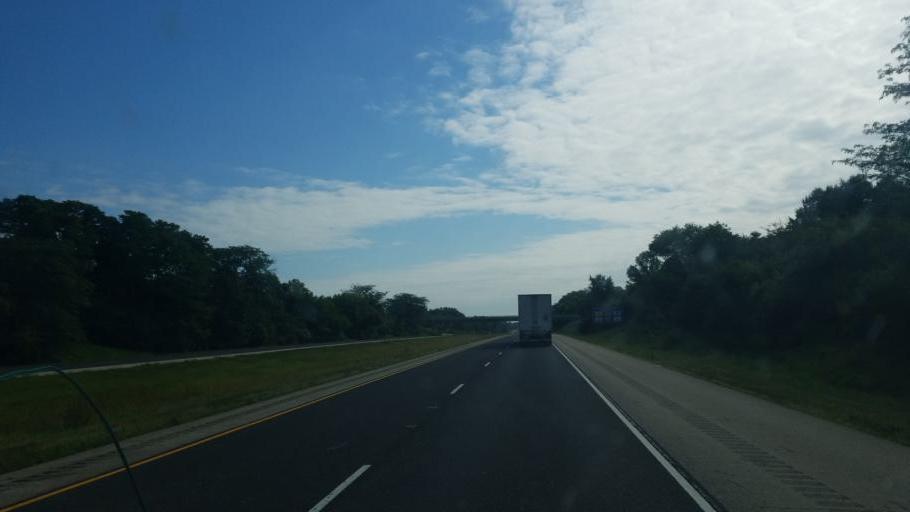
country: US
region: Illinois
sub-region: Clark County
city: Marshall
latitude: 39.4096
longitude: -87.7258
